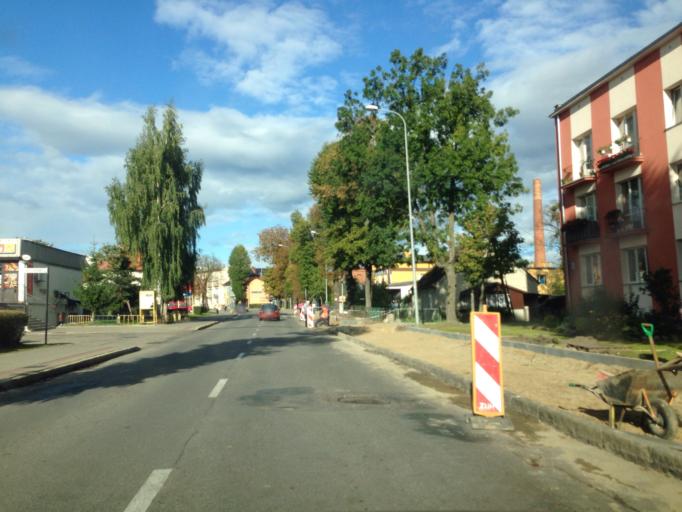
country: PL
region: Warmian-Masurian Voivodeship
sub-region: Powiat ilawski
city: Susz
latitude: 53.7118
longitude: 19.3341
